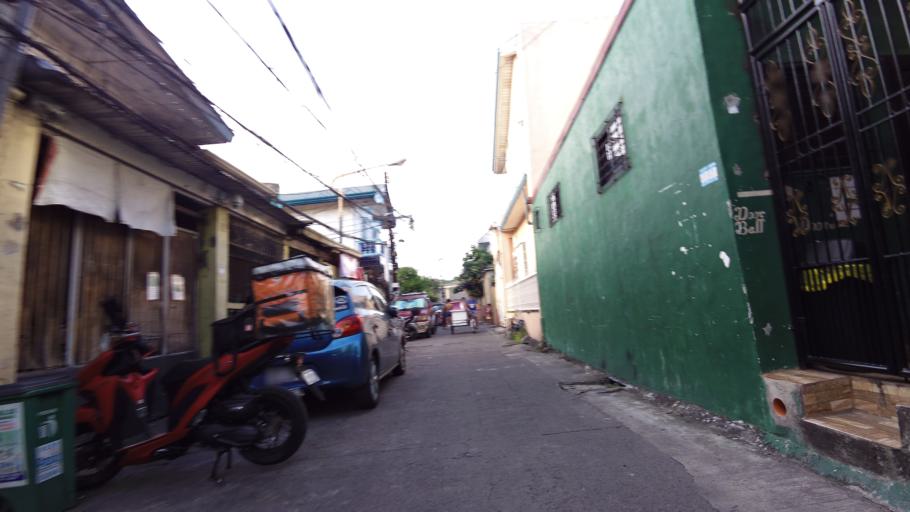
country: PH
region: Metro Manila
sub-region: Pasig
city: Pasig City
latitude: 14.5682
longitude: 121.0781
